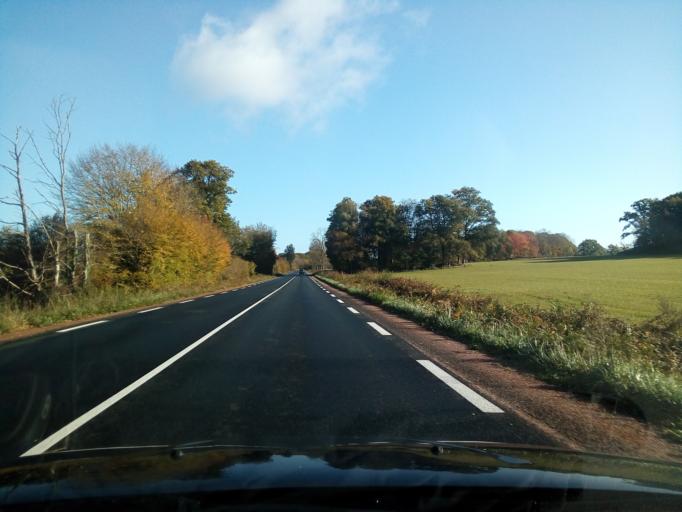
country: FR
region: Limousin
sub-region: Departement de la Haute-Vienne
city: Magnac-Laval
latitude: 46.1763
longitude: 1.1534
